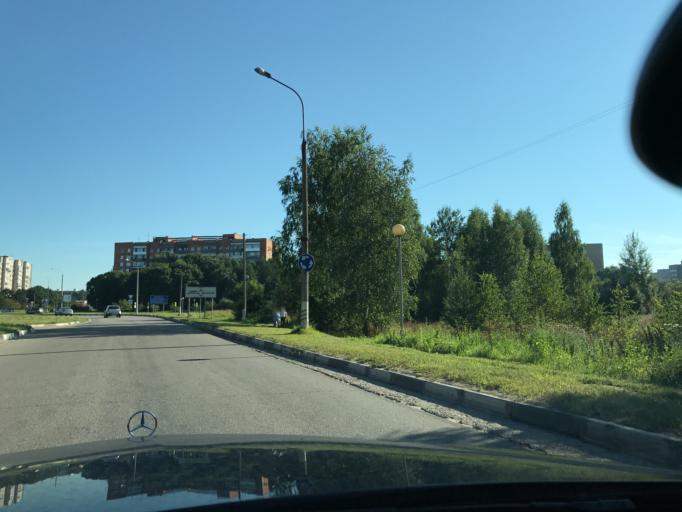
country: RU
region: Moskovskaya
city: Chernogolovka
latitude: 56.0052
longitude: 38.3724
